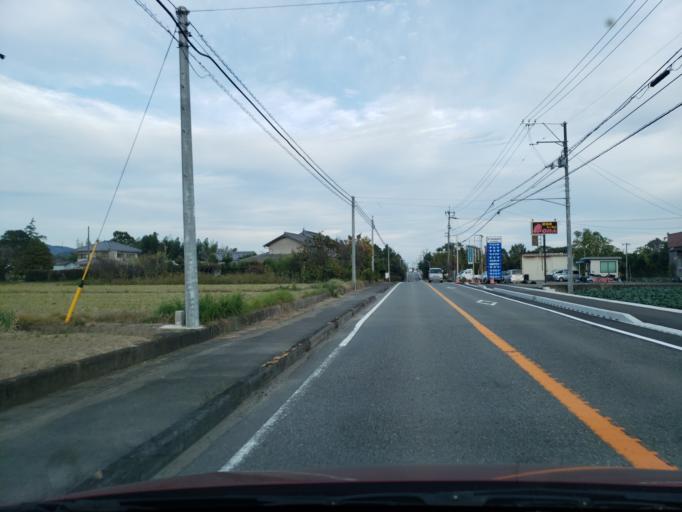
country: JP
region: Tokushima
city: Kamojimacho-jogejima
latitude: 34.0808
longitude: 134.2608
